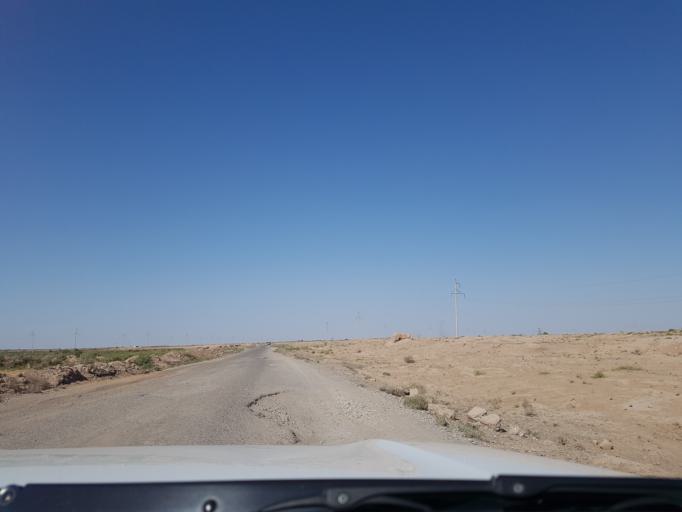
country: IR
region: Razavi Khorasan
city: Sarakhs
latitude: 36.5267
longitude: 61.2422
